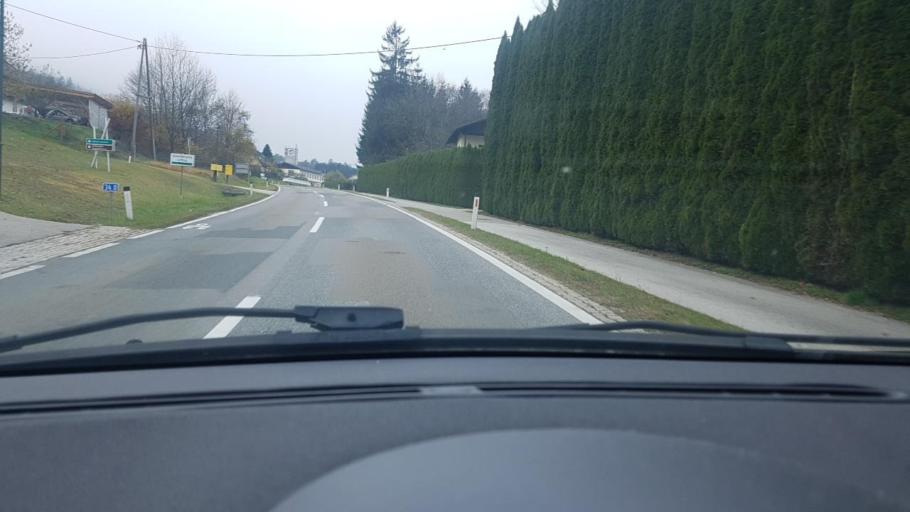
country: AT
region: Carinthia
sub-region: Politischer Bezirk Wolfsberg
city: Lavamund
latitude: 46.6436
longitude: 14.9340
